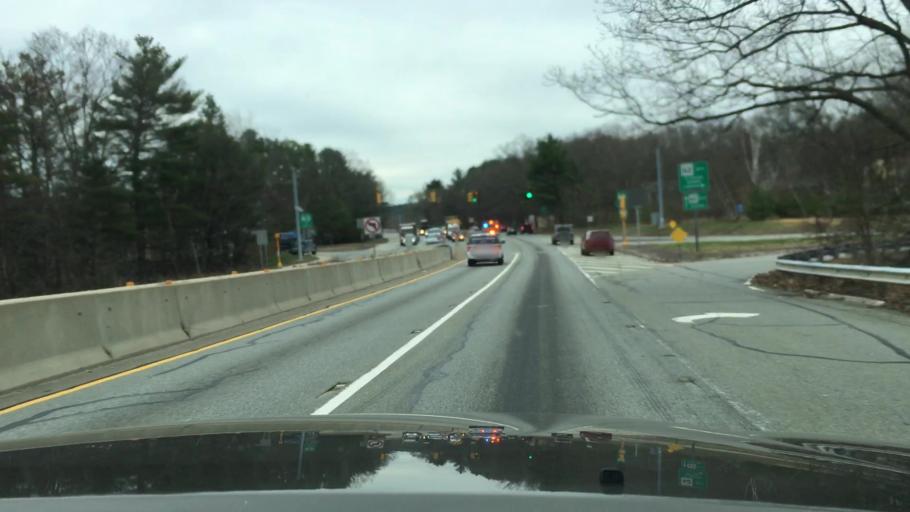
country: US
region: Massachusetts
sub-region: Middlesex County
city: West Concord
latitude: 42.4566
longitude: -71.3800
